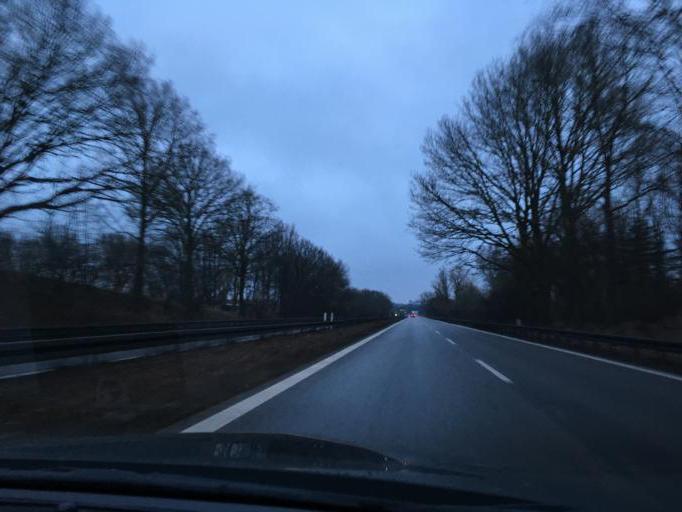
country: DK
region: Capital Region
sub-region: Horsholm Kommune
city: Horsholm
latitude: 55.8875
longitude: 12.4776
